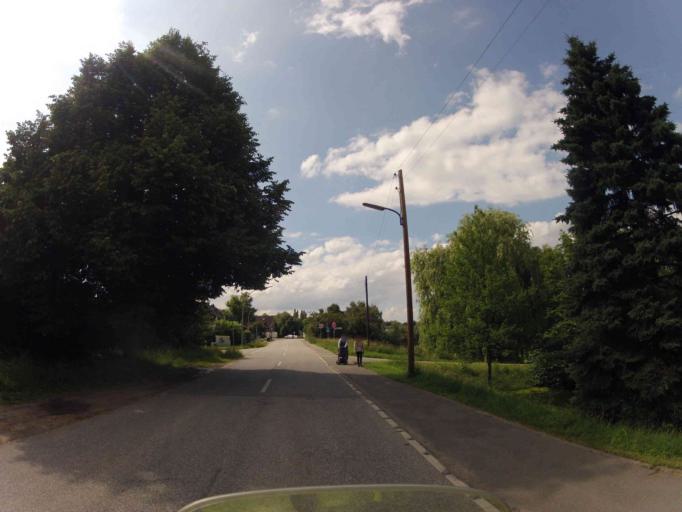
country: DE
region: Hamburg
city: Rothenburgsort
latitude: 53.5009
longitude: 10.0816
